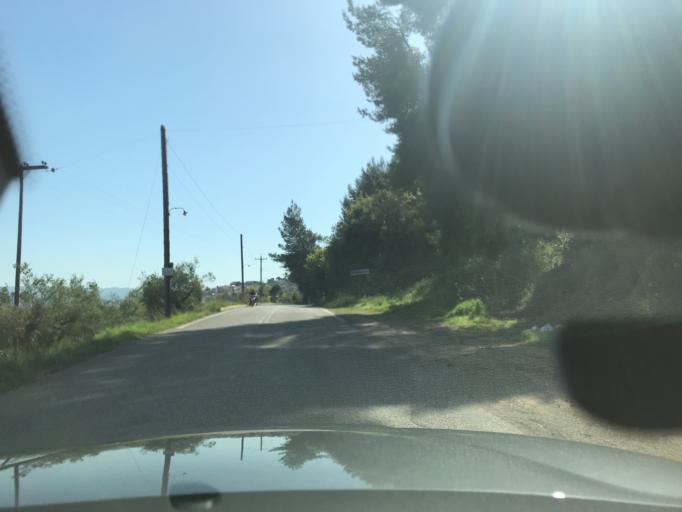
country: GR
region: West Greece
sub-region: Nomos Ileias
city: Alfiousa
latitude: 37.6400
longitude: 21.5277
